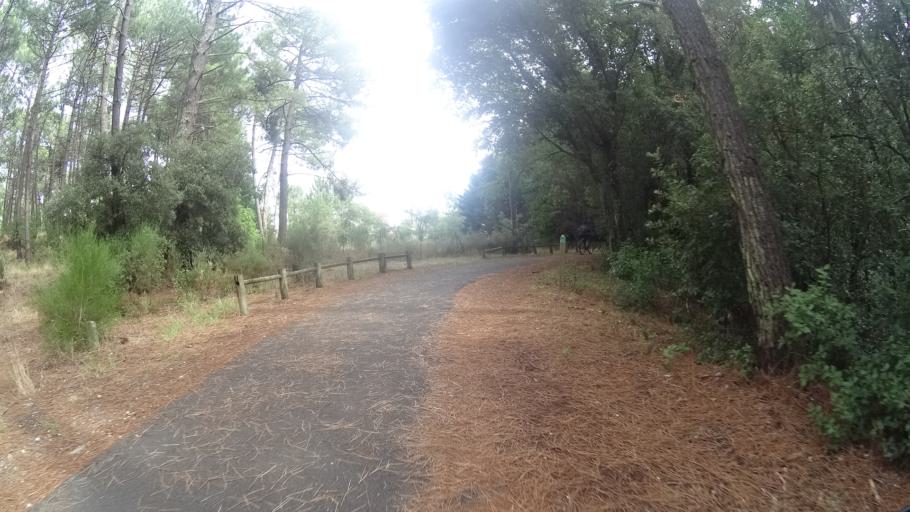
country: FR
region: Aquitaine
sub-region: Departement de la Gironde
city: Lacanau
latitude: 45.0042
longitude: -1.1377
